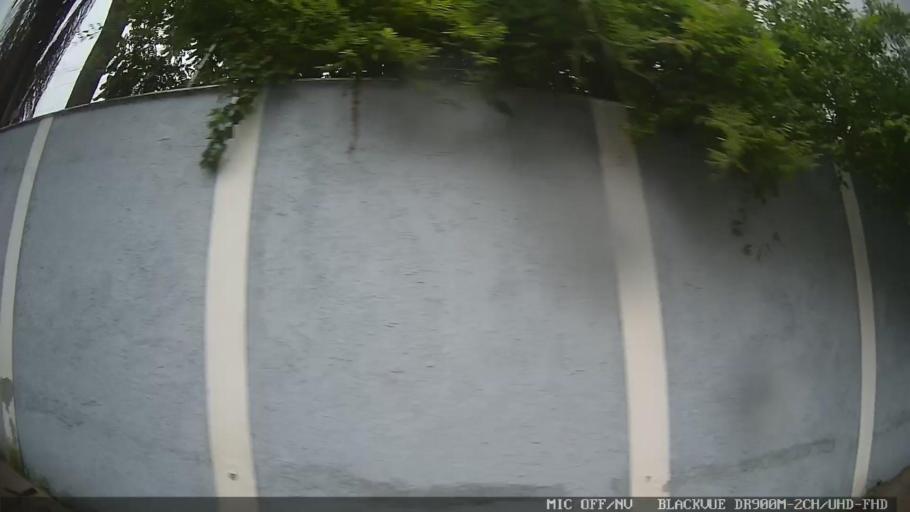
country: BR
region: Sao Paulo
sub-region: Mogi das Cruzes
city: Mogi das Cruzes
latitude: -23.5204
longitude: -46.1765
